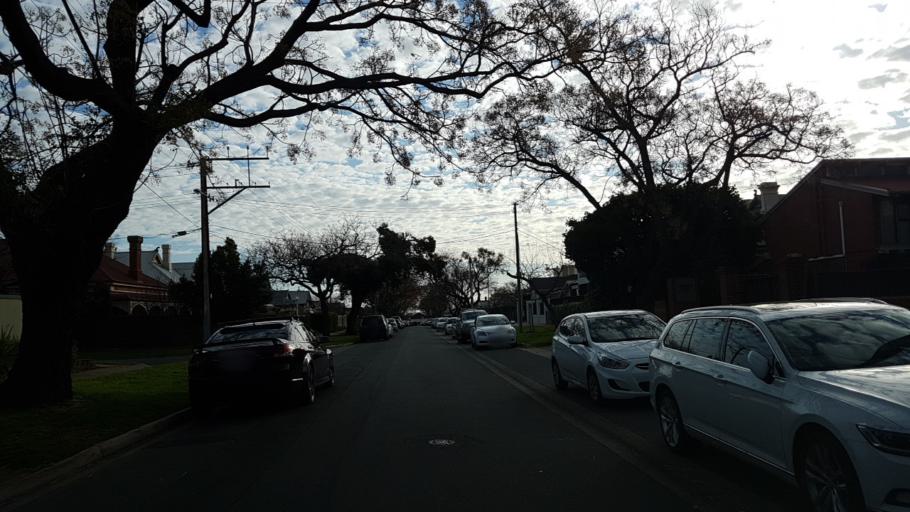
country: AU
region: South Australia
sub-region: Prospect
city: Prospect
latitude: -34.8869
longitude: 138.5979
